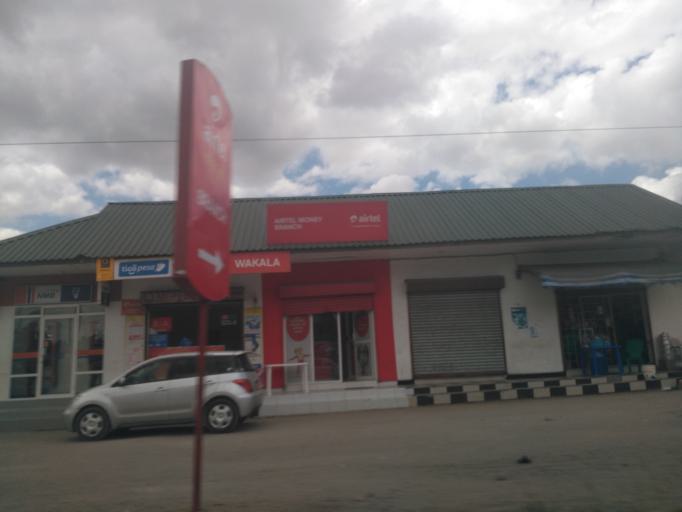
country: TZ
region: Dar es Salaam
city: Dar es Salaam
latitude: -6.8922
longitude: 39.2250
